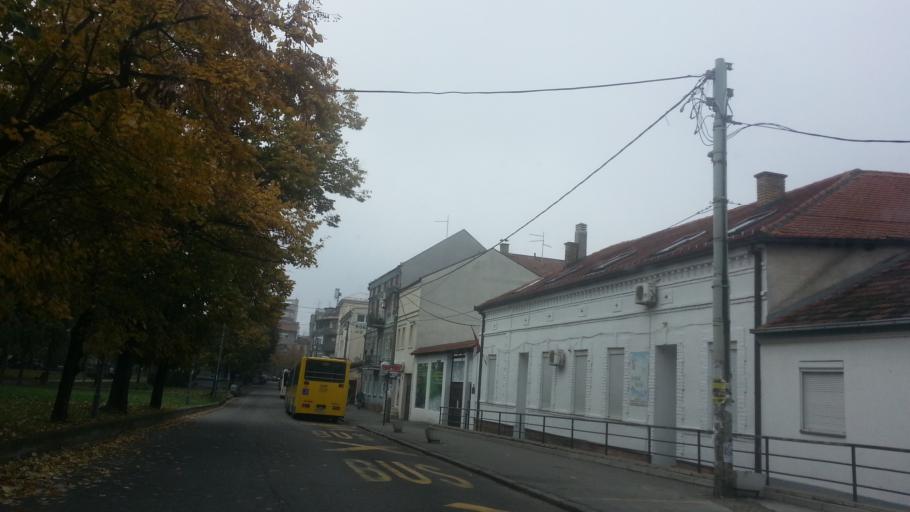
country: RS
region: Central Serbia
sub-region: Belgrade
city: Zemun
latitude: 44.8438
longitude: 20.4163
